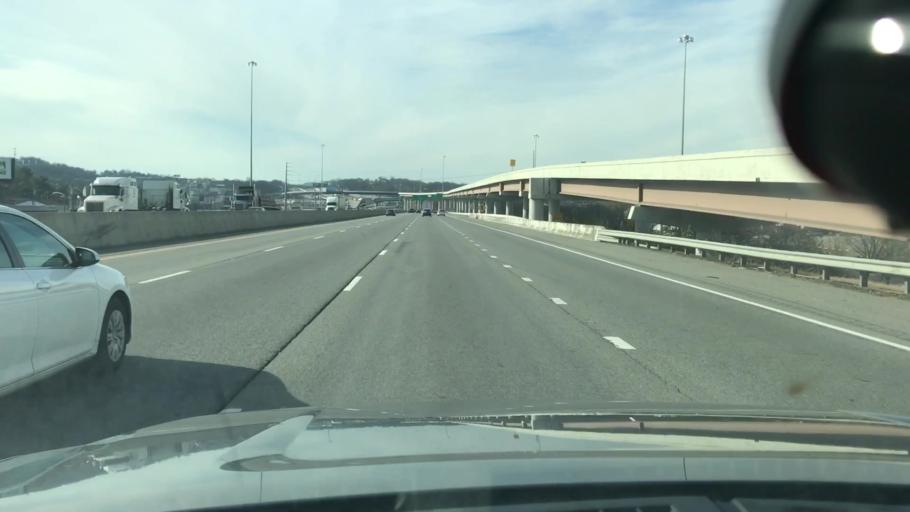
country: US
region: Tennessee
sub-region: Davidson County
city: Belle Meade
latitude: 36.1544
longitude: -86.8435
